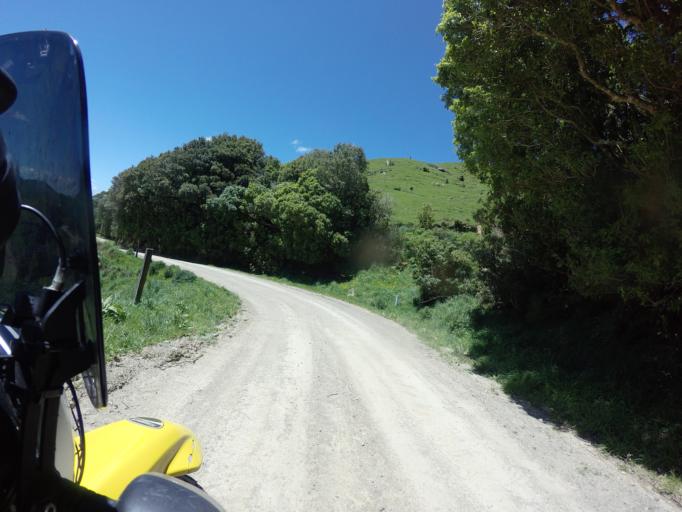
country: NZ
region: Bay of Plenty
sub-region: Opotiki District
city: Opotiki
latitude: -38.4055
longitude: 177.4488
